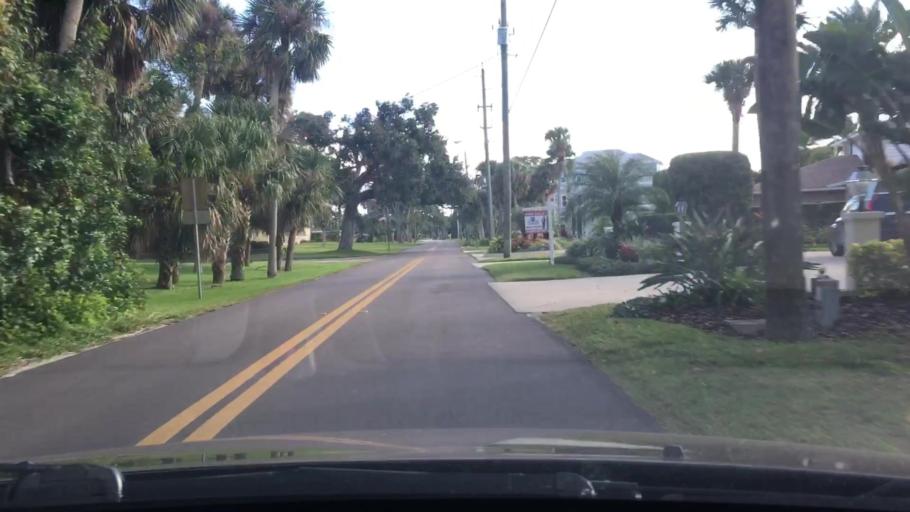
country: US
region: Florida
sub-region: Volusia County
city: Ormond-by-the-Sea
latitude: 29.3687
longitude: -81.0818
